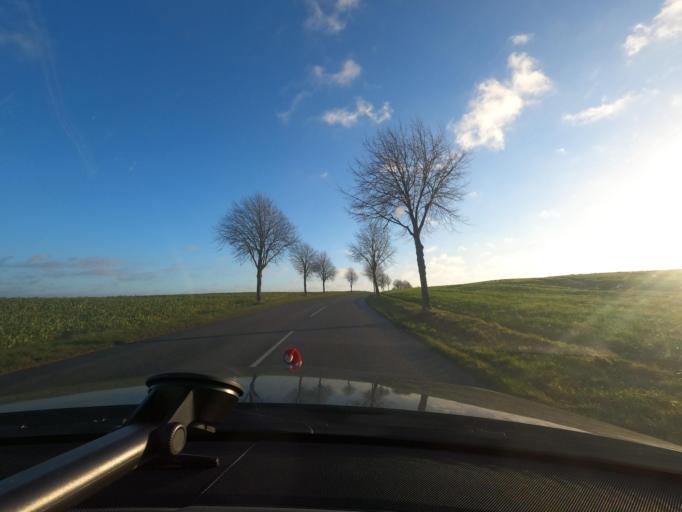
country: DK
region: South Denmark
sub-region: Sonderborg Kommune
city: Broager
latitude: 54.8956
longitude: 9.6833
